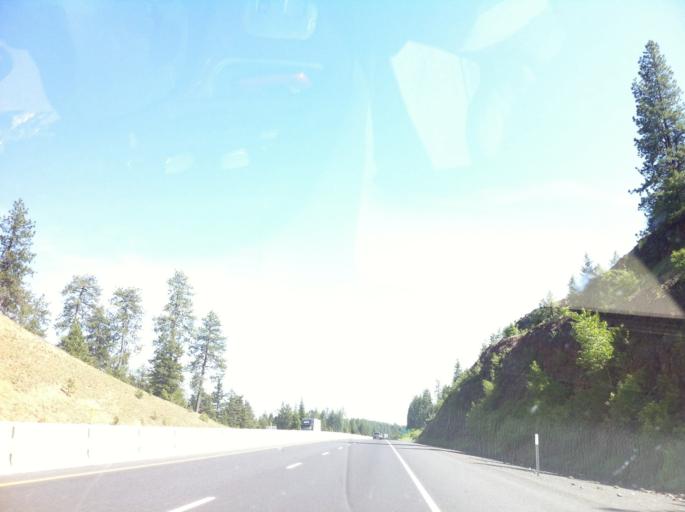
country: US
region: Oregon
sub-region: Umatilla County
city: Mission
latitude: 45.4795
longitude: -118.4014
